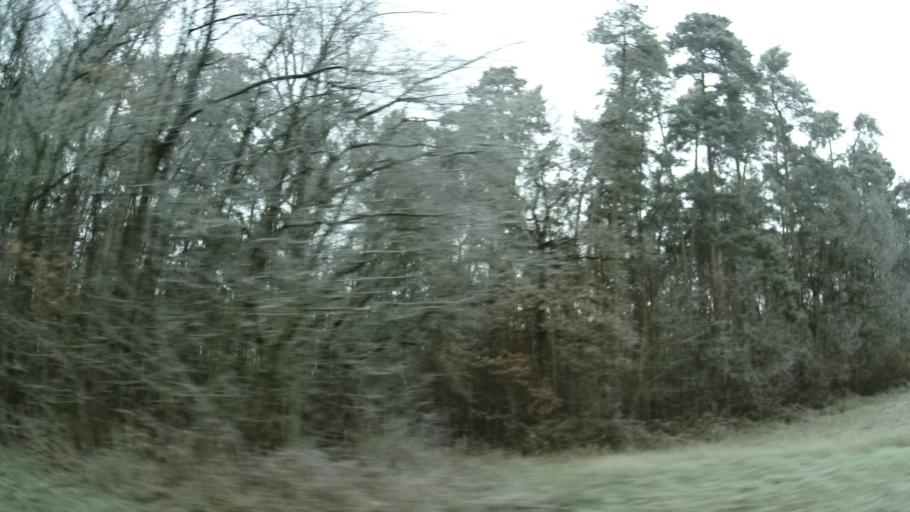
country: DE
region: Bavaria
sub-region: Regierungsbezirk Unterfranken
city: Volkach
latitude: 49.8348
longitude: 10.2465
